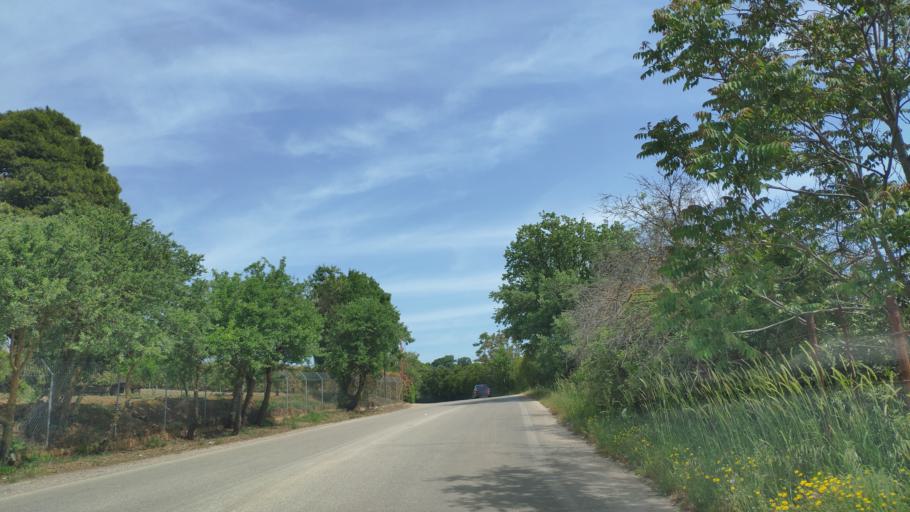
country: GR
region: Attica
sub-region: Nomarchia Anatolikis Attikis
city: Agios Stefanos
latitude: 38.1759
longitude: 23.8599
